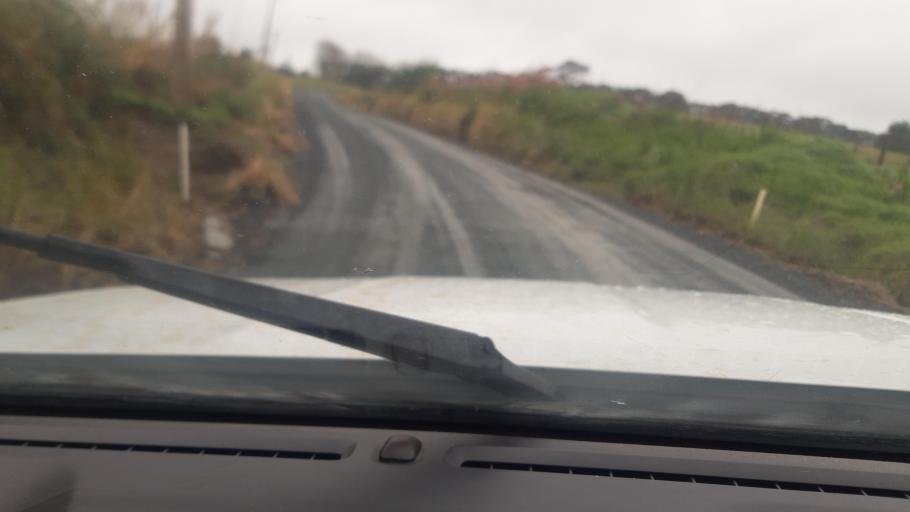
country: NZ
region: Northland
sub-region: Far North District
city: Kaitaia
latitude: -34.9803
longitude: 173.1949
